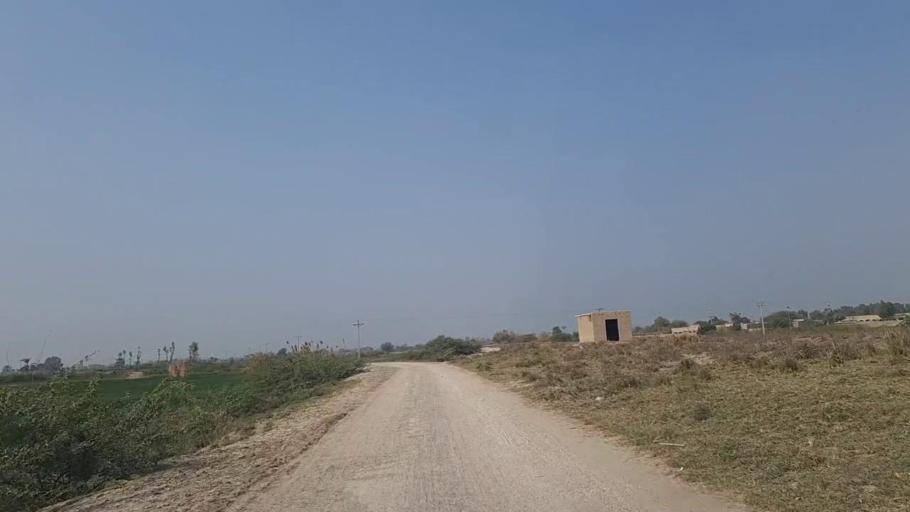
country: PK
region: Sindh
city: Daur
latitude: 26.4482
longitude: 68.4493
